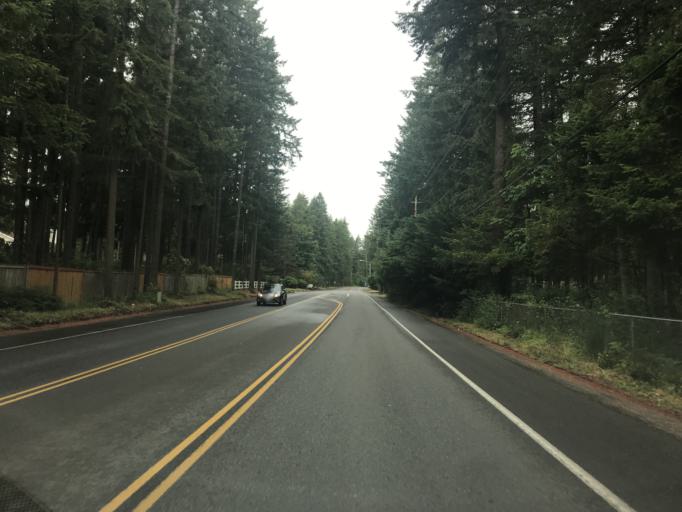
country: US
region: Washington
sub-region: King County
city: Lake Morton-Berrydale
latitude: 47.3422
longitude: -122.0644
